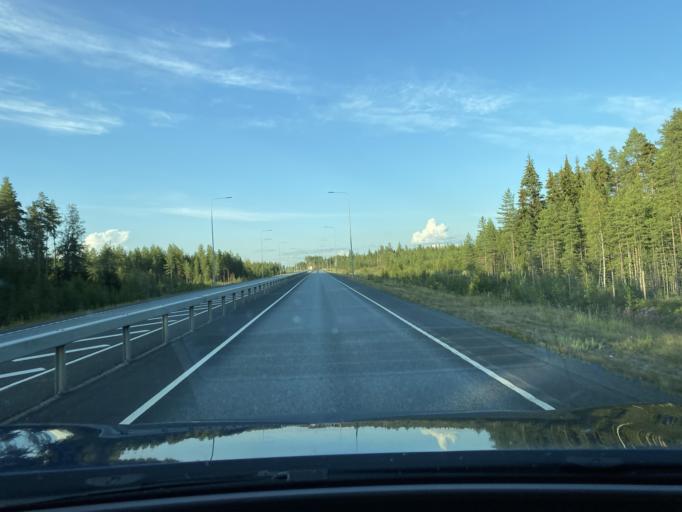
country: FI
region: Southern Ostrobothnia
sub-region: Seinaejoki
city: Seinaejoki
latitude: 62.7105
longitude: 22.8411
